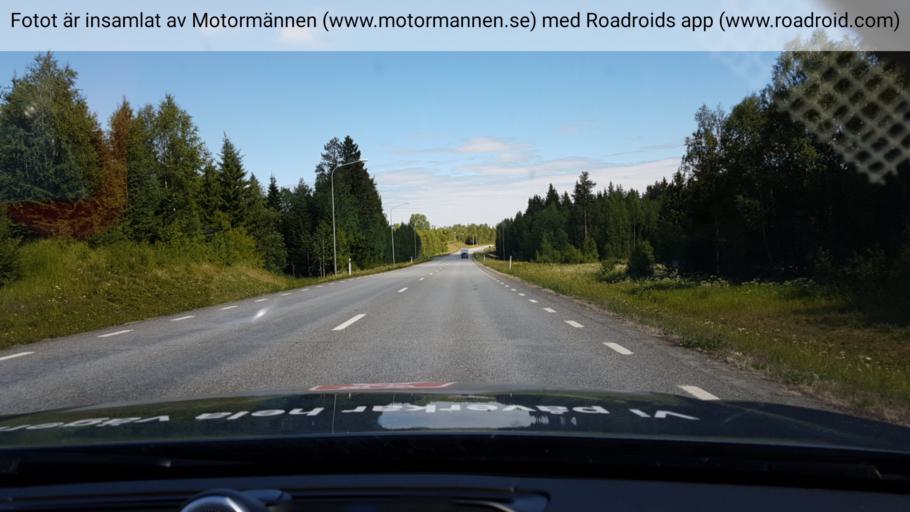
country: SE
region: Jaemtland
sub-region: Stroemsunds Kommun
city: Stroemsund
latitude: 63.6768
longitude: 15.3967
